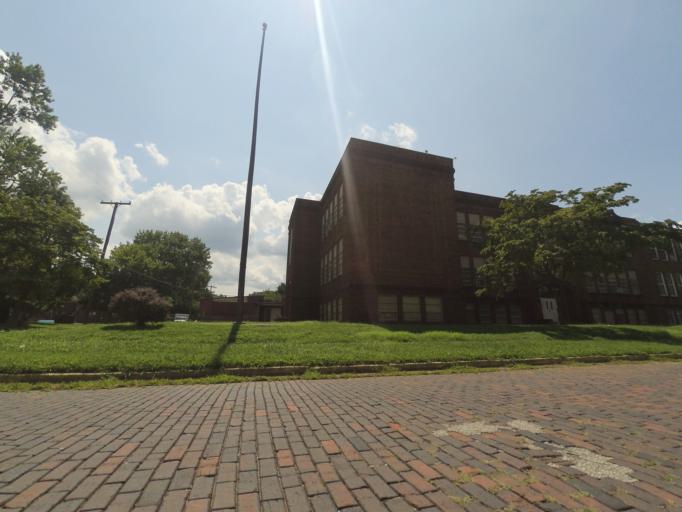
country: US
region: West Virginia
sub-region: Cabell County
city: Huntington
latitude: 38.4120
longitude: -82.4727
